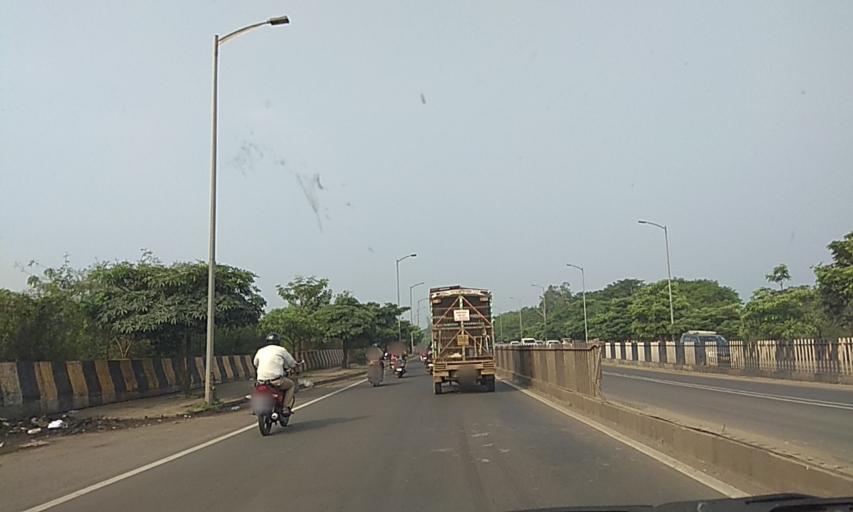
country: IN
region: Maharashtra
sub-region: Pune Division
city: Shivaji Nagar
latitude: 18.5411
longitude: 73.8695
